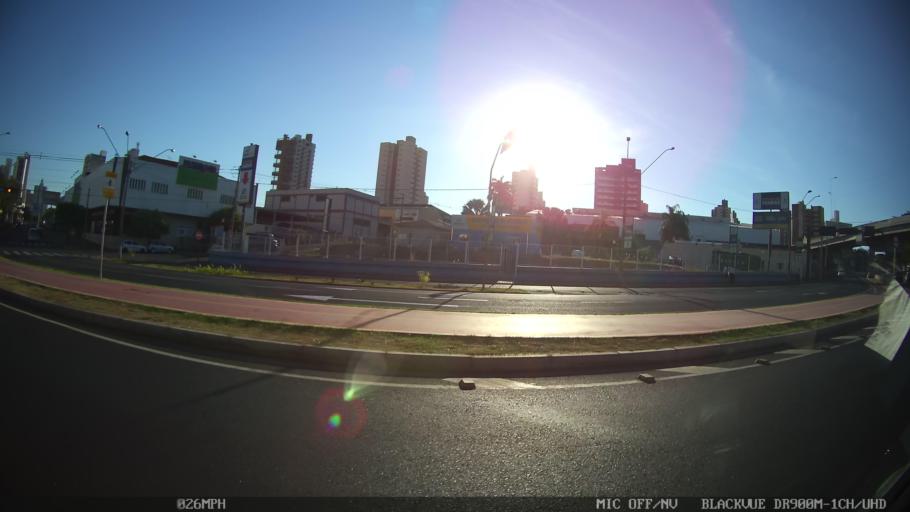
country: BR
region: Sao Paulo
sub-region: Sao Jose Do Rio Preto
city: Sao Jose do Rio Preto
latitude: -20.8066
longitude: -49.3793
